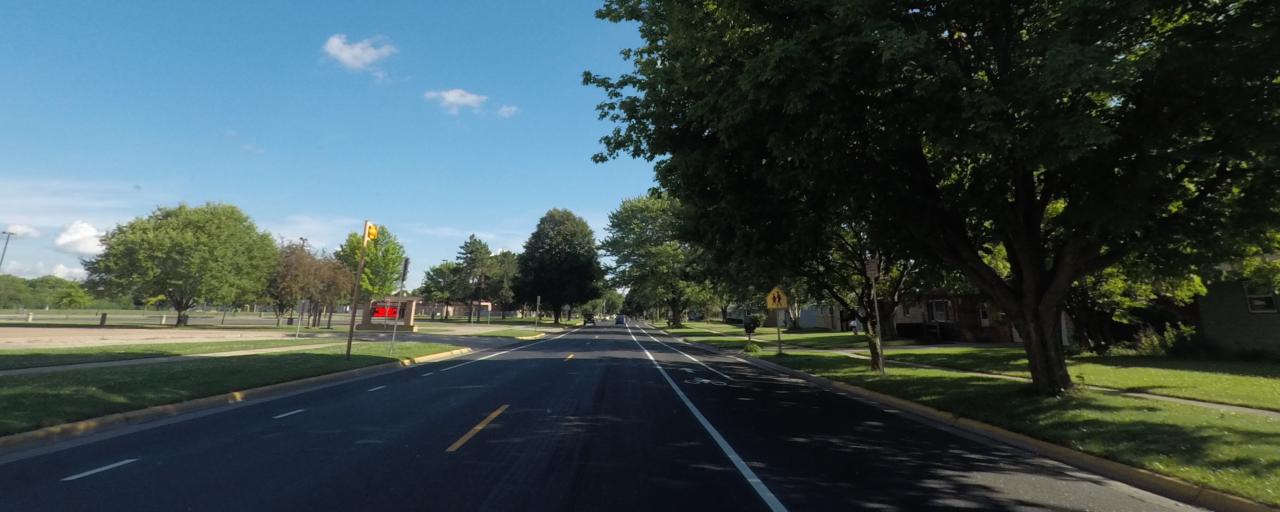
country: US
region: Wisconsin
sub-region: Rock County
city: Janesville
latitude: 42.6927
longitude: -88.9876
